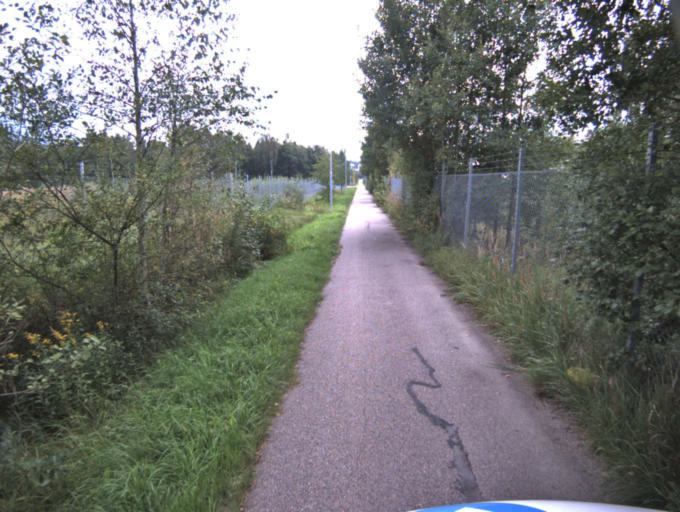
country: SE
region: Vaestra Goetaland
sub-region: Ulricehamns Kommun
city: Ulricehamn
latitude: 57.8066
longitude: 13.4122
